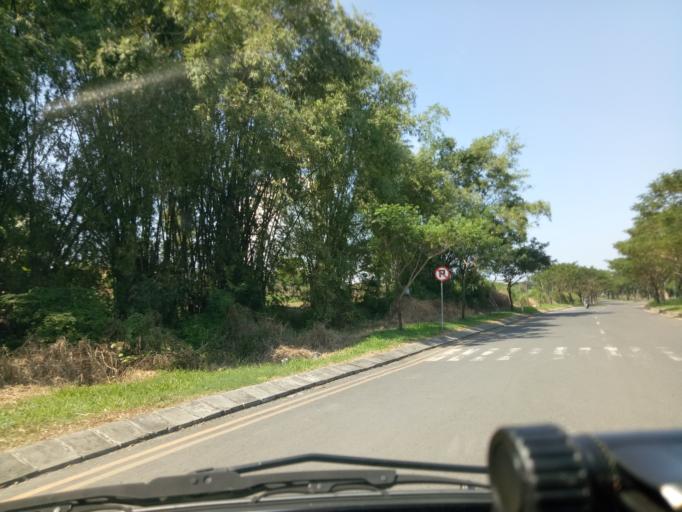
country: ID
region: East Java
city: Driyorejo
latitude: -7.2816
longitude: 112.6362
